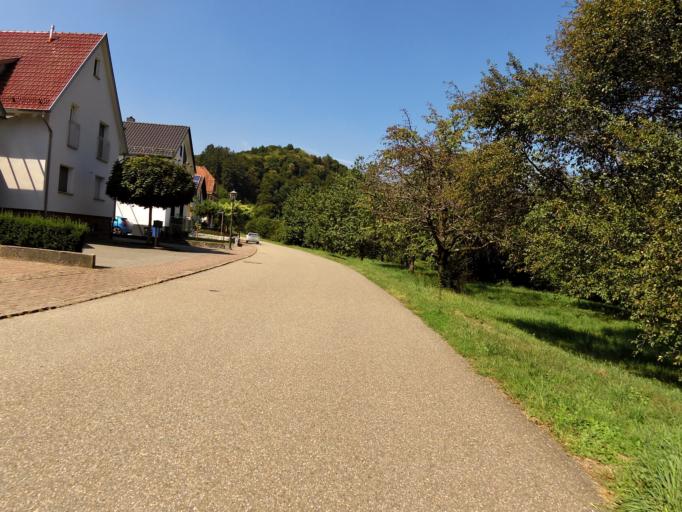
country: DE
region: Baden-Wuerttemberg
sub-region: Karlsruhe Region
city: Neckargerach
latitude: 49.3925
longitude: 9.0739
